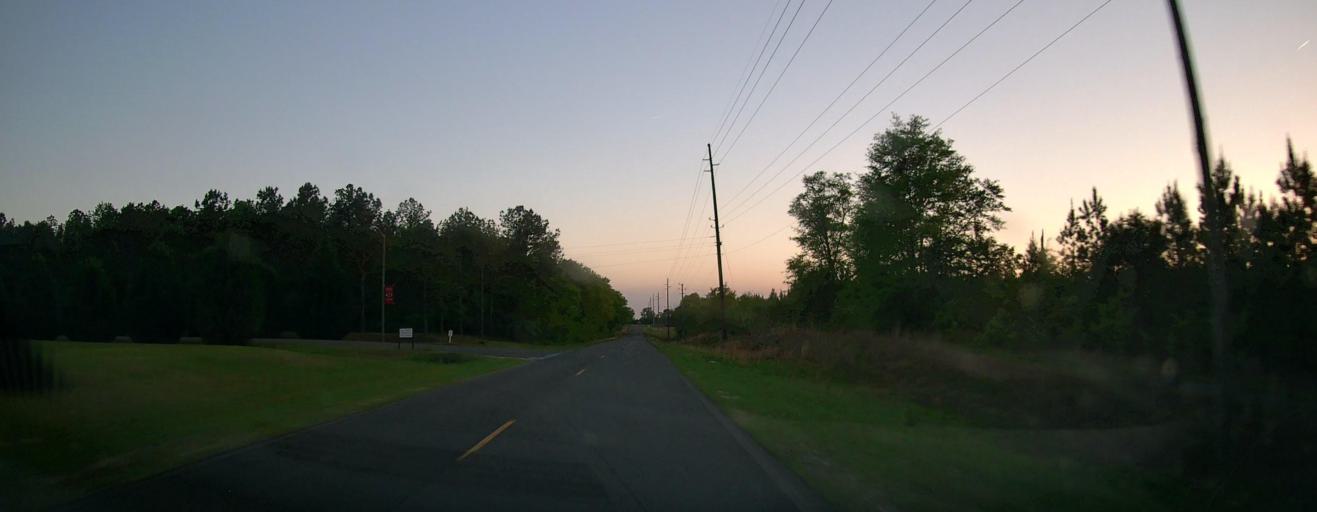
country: US
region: Georgia
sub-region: Marion County
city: Buena Vista
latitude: 32.2877
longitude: -84.5371
